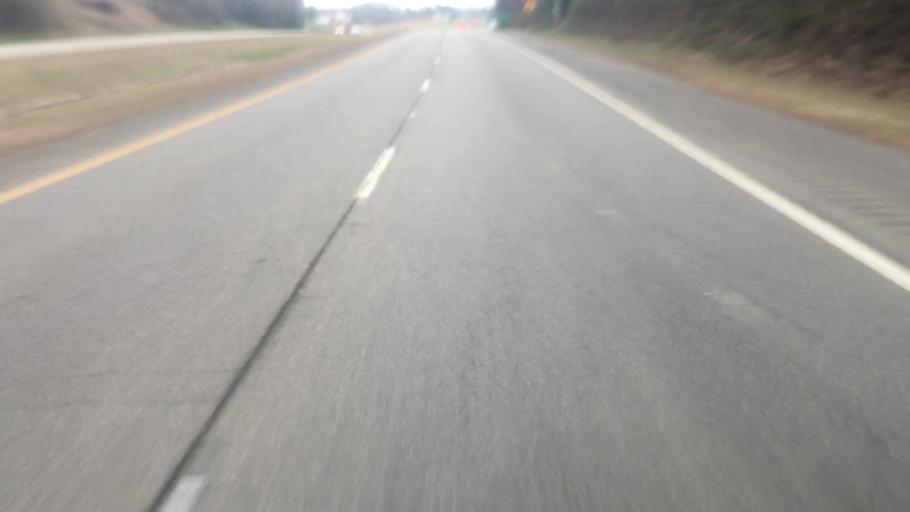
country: US
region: Alabama
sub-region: Walker County
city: Sumiton
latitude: 33.7475
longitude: -87.0540
